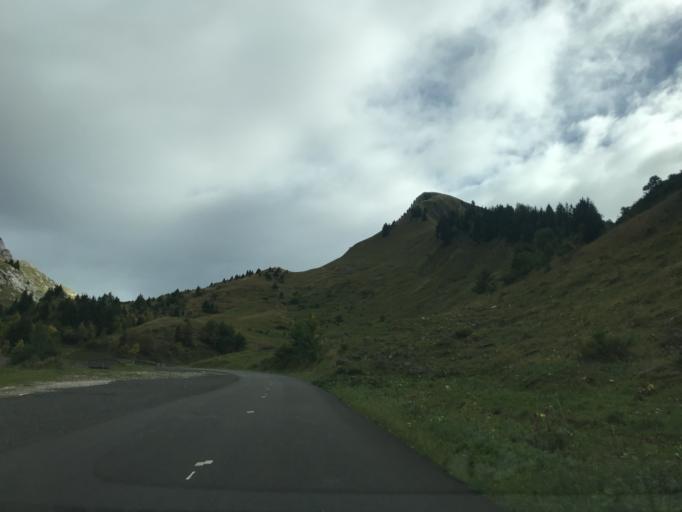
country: FR
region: Rhone-Alpes
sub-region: Departement de la Haute-Savoie
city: Le Grand-Bornand
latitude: 45.9869
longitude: 6.4694
